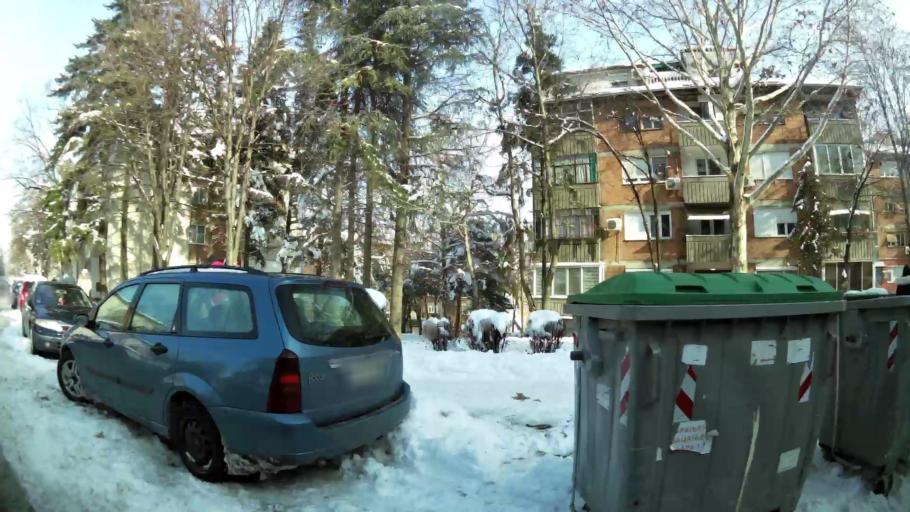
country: RS
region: Central Serbia
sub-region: Belgrade
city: Palilula
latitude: 44.8027
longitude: 20.5227
